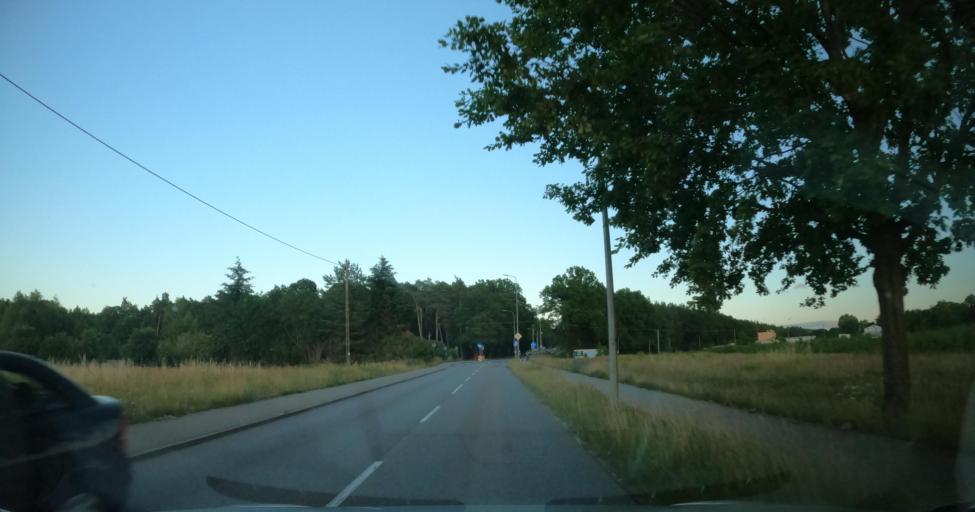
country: PL
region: Pomeranian Voivodeship
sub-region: Powiat leborski
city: Lebork
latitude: 54.5265
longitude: 17.7725
